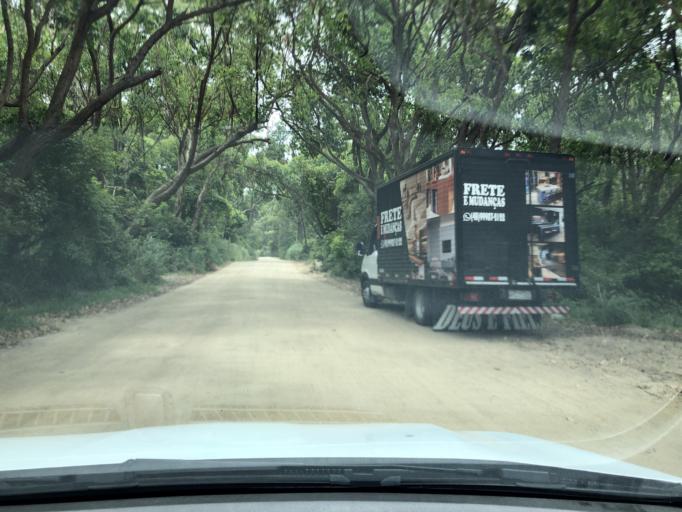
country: BR
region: Santa Catarina
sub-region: Florianopolis
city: Lagoa
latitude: -27.5231
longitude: -48.4182
